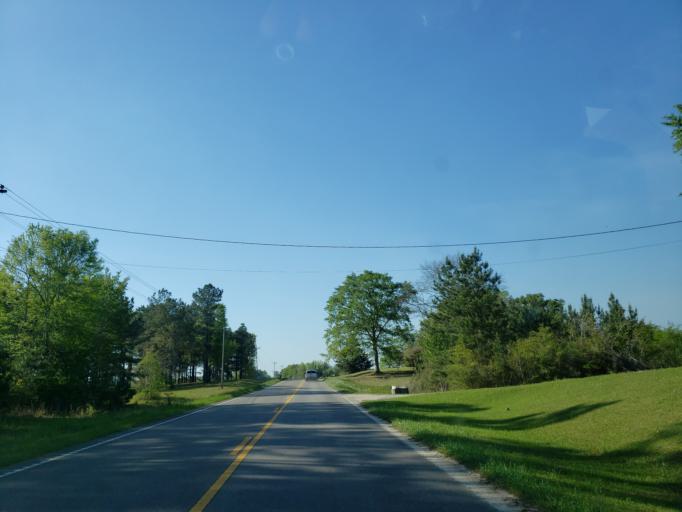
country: US
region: Mississippi
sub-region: Perry County
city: Richton
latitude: 31.4556
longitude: -88.9807
